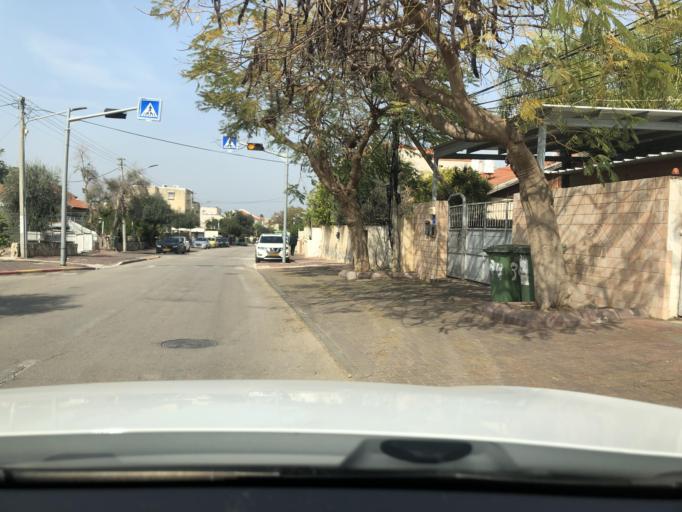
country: IL
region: Central District
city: Rosh Ha'Ayin
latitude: 32.0937
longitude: 34.9503
